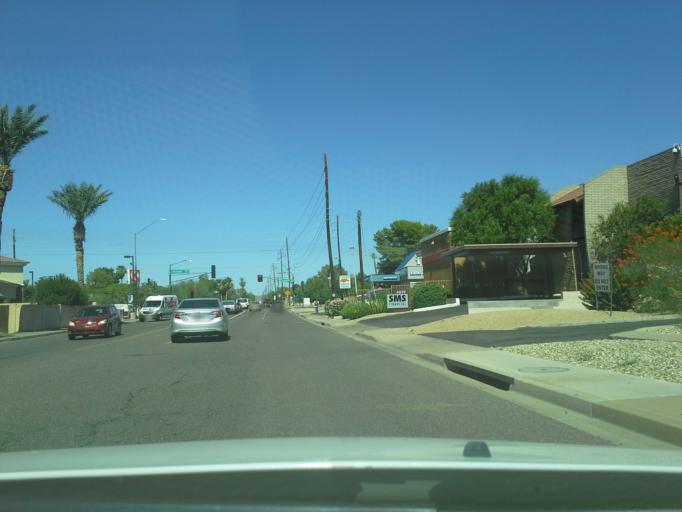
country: US
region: Arizona
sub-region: Maricopa County
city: Phoenix
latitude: 33.5371
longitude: -112.0563
